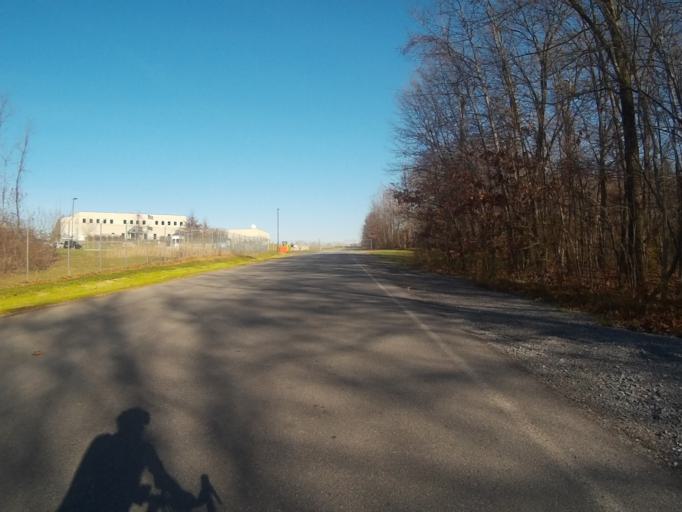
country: US
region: Pennsylvania
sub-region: Centre County
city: Houserville
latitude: 40.8408
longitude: -77.8541
